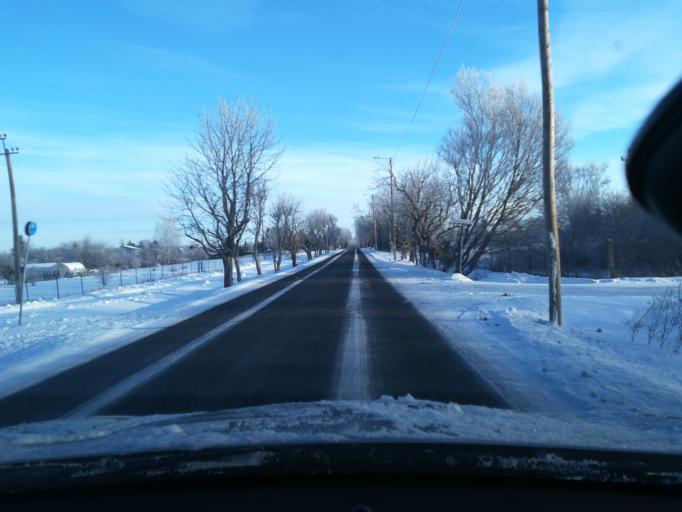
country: EE
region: Harju
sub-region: Keila linn
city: Keila
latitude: 59.3972
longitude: 24.3077
